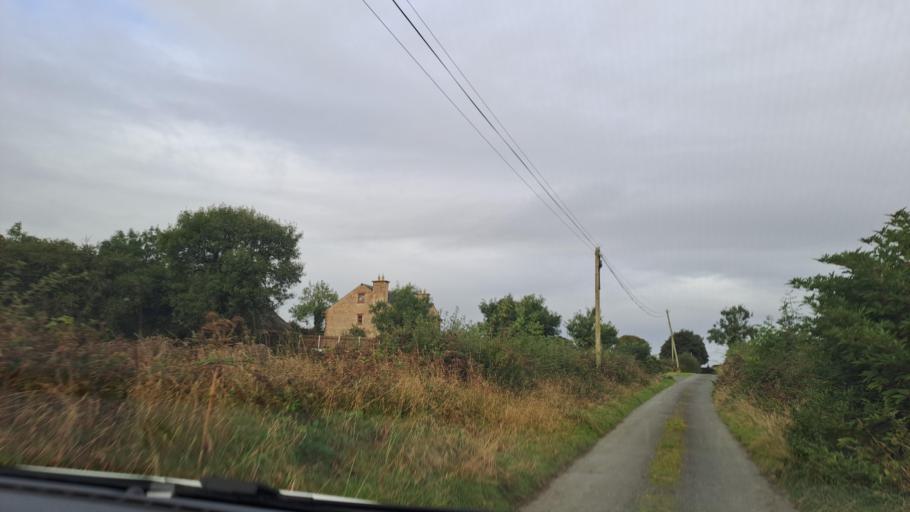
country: IE
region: Ulster
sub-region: An Cabhan
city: Kingscourt
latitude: 53.9948
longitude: -6.8623
